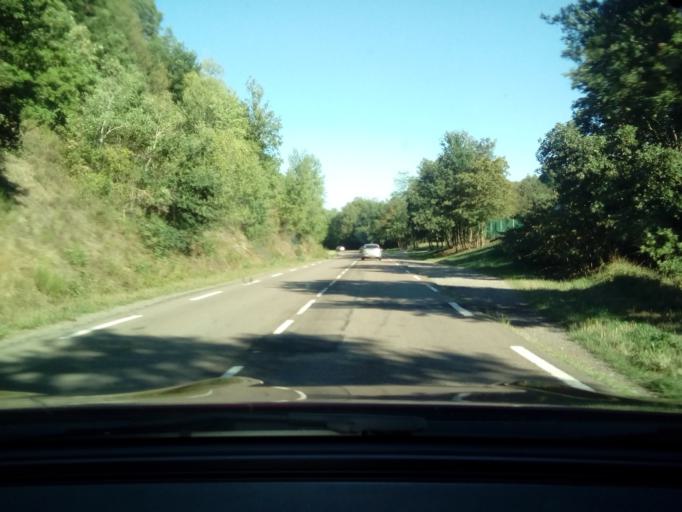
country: FR
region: Rhone-Alpes
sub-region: Departement du Rhone
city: Saint-Verand
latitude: 45.9022
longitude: 4.5490
